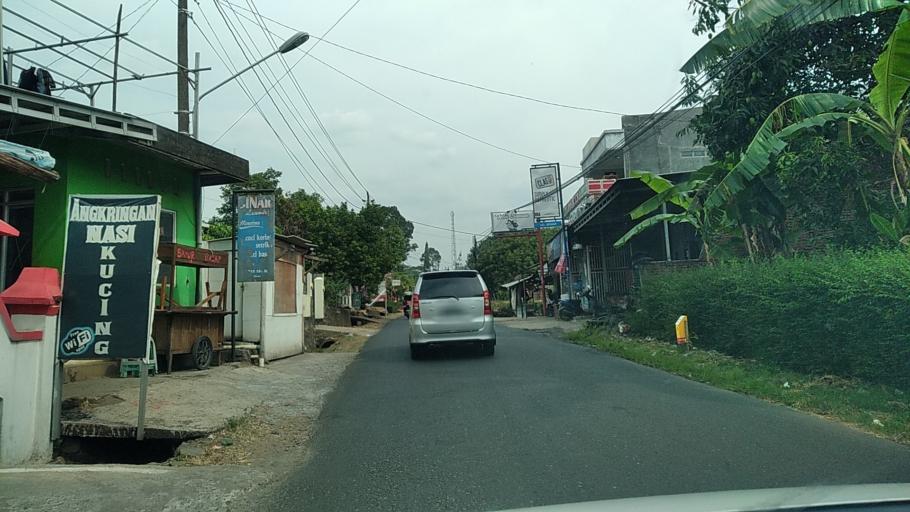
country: ID
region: Central Java
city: Ungaran
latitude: -7.0862
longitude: 110.3874
